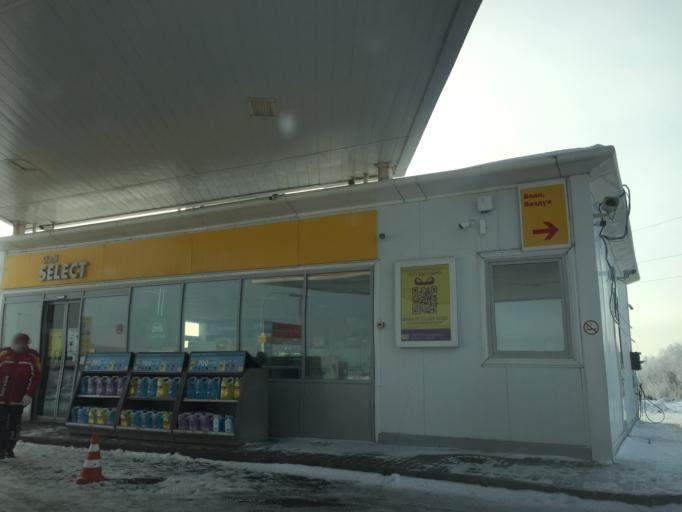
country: RU
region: St.-Petersburg
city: Shushary
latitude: 59.7924
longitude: 30.3915
